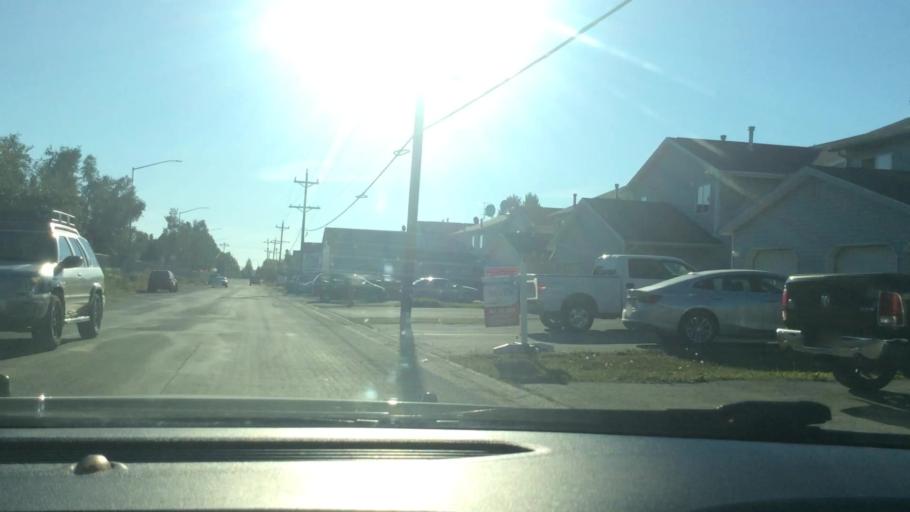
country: US
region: Alaska
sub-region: Anchorage Municipality
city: Anchorage
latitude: 61.2169
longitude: -149.7726
